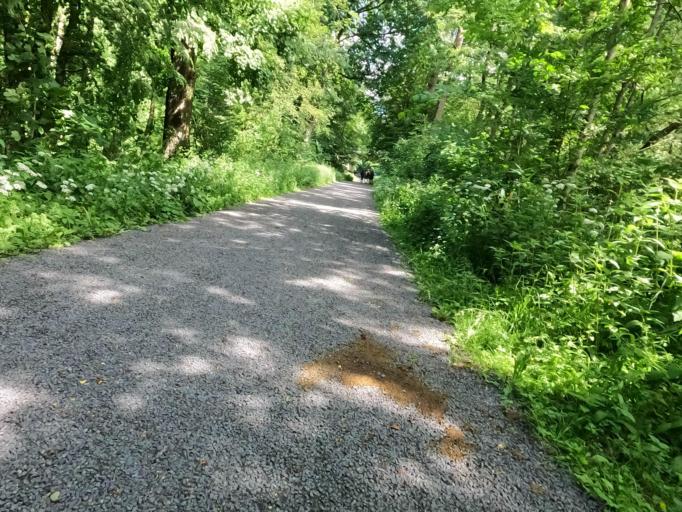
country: DE
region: Rheinland-Pfalz
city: Muschenbach
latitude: 50.6833
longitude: 7.7979
